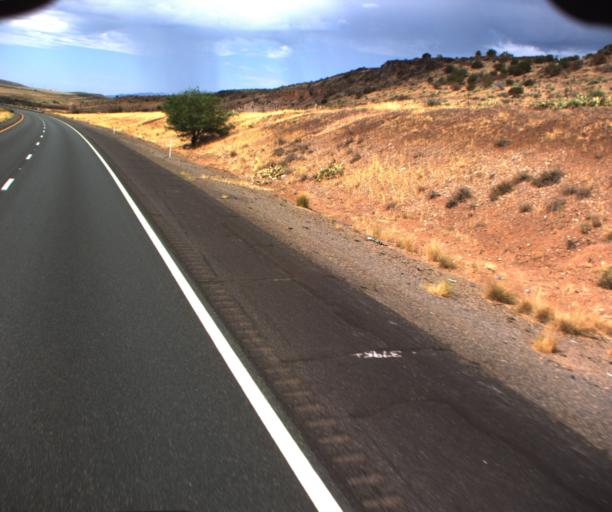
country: US
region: Arizona
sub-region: Yavapai County
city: Cordes Lakes
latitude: 34.4569
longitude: -112.0337
